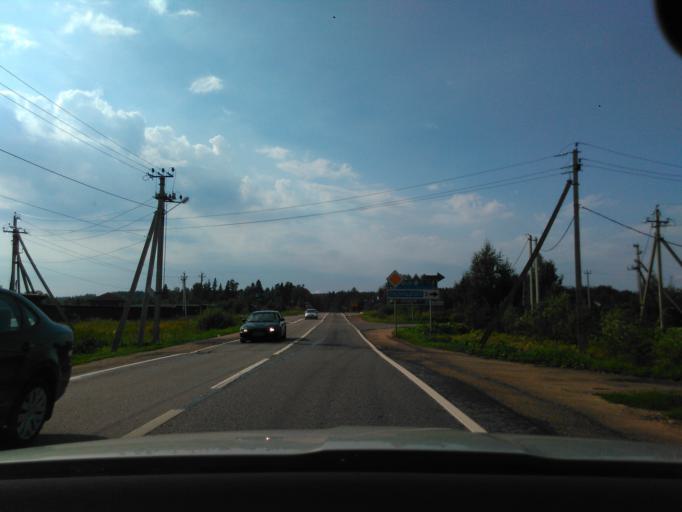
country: RU
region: Moskovskaya
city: Solnechnogorsk
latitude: 56.1397
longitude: 36.8414
